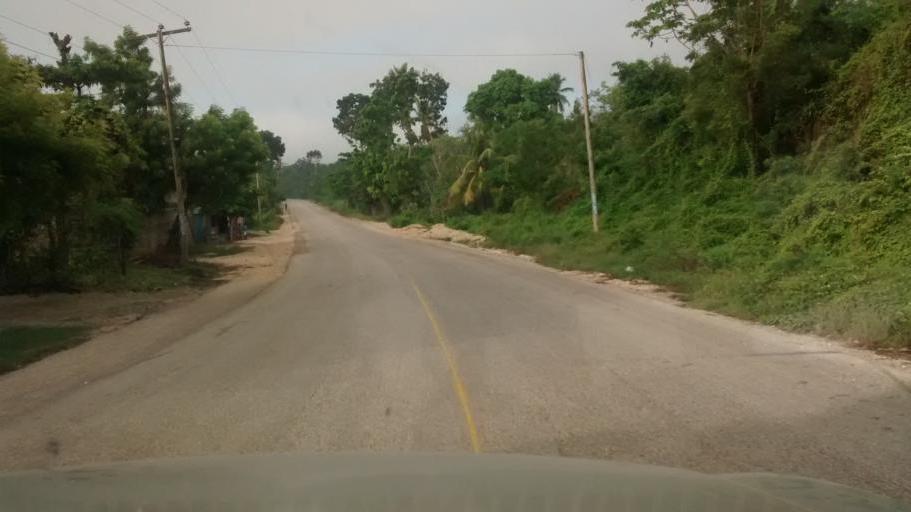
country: HT
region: Nippes
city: Miragoane
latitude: 18.3742
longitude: -73.1265
